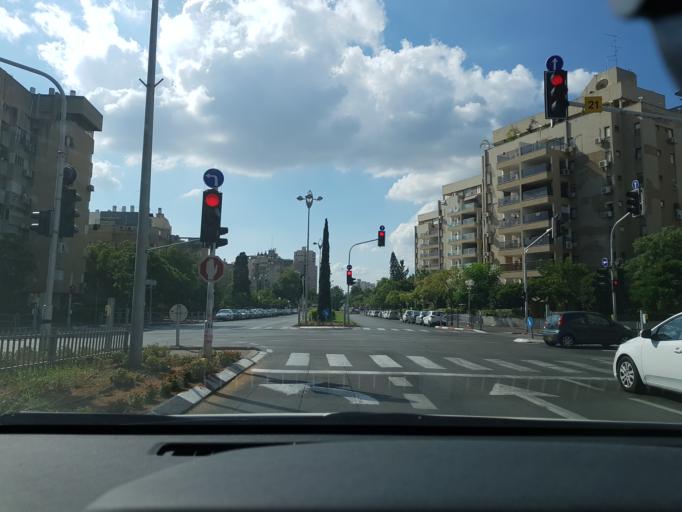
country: IL
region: Tel Aviv
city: Holon
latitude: 32.0103
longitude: 34.7923
